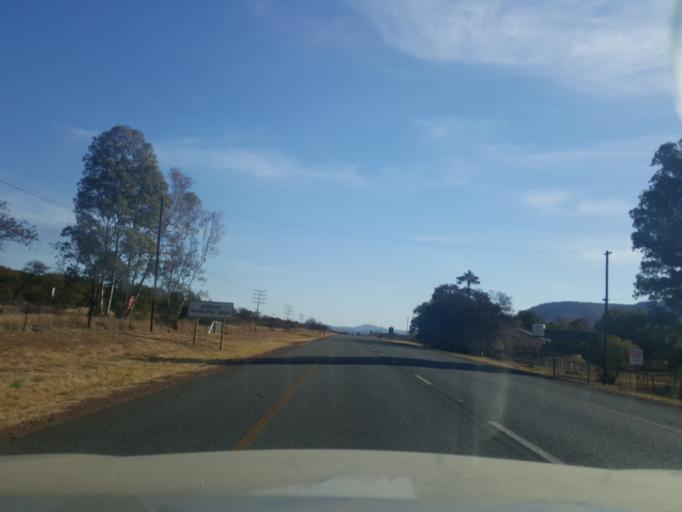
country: ZA
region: North-West
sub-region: Ngaka Modiri Molema District Municipality
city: Zeerust
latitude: -25.5314
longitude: 26.1413
